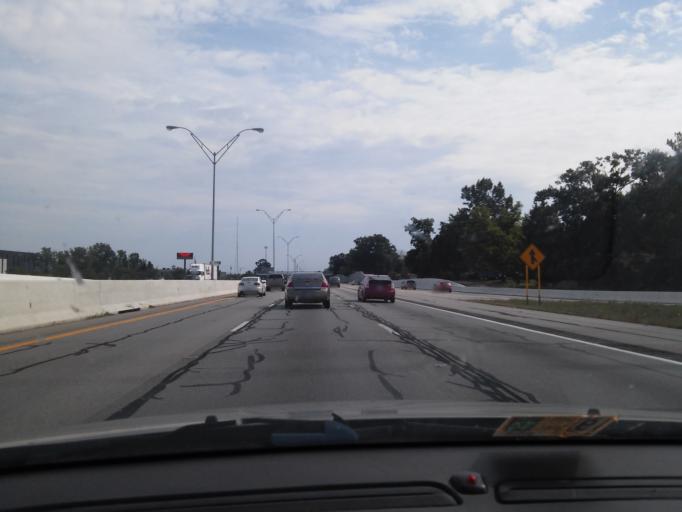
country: US
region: Ohio
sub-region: Montgomery County
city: Northridge
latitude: 39.8391
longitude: -84.1898
